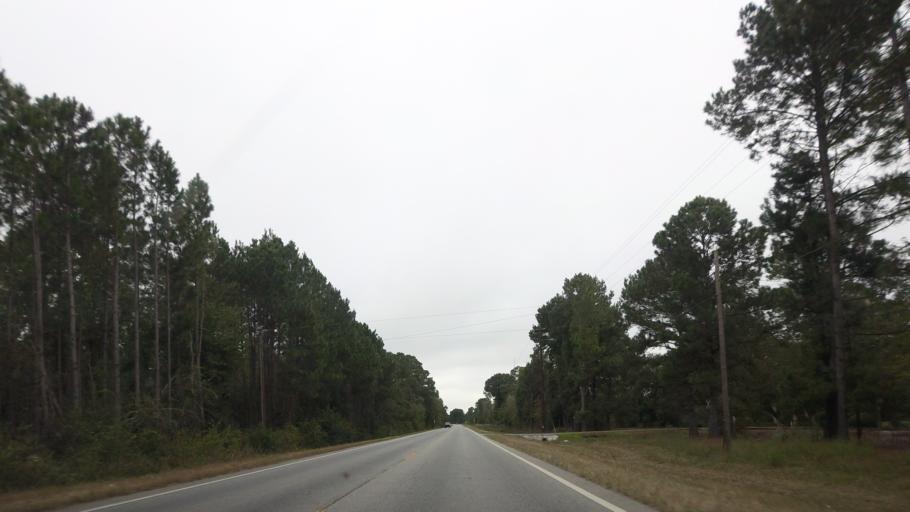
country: US
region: Georgia
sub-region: Berrien County
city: Ray City
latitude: 31.1378
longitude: -83.2164
